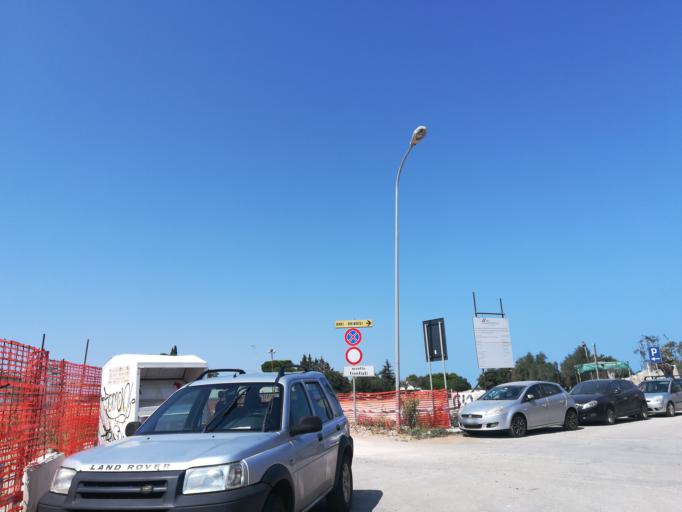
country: IT
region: Apulia
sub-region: Provincia di Bari
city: Polignano a Mare
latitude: 40.9951
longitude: 17.2136
